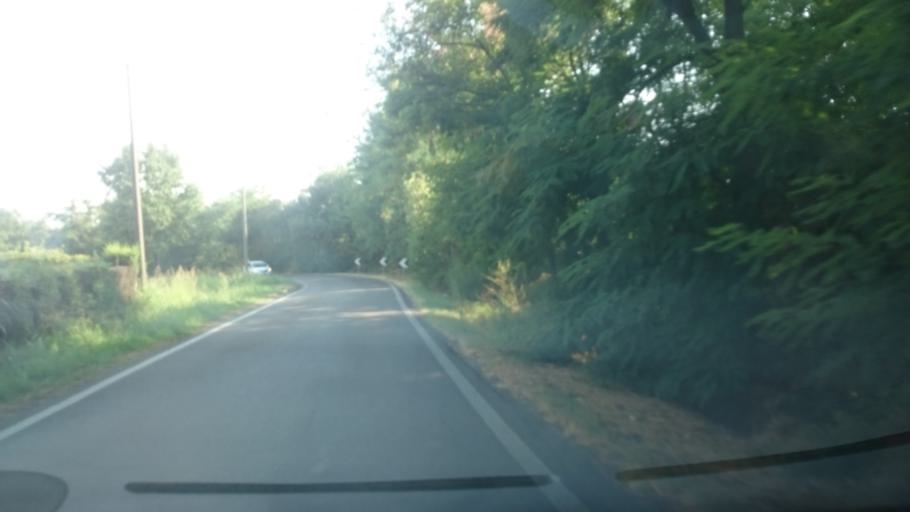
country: IT
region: Emilia-Romagna
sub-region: Provincia di Reggio Emilia
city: Arceto
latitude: 44.6055
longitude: 10.7260
